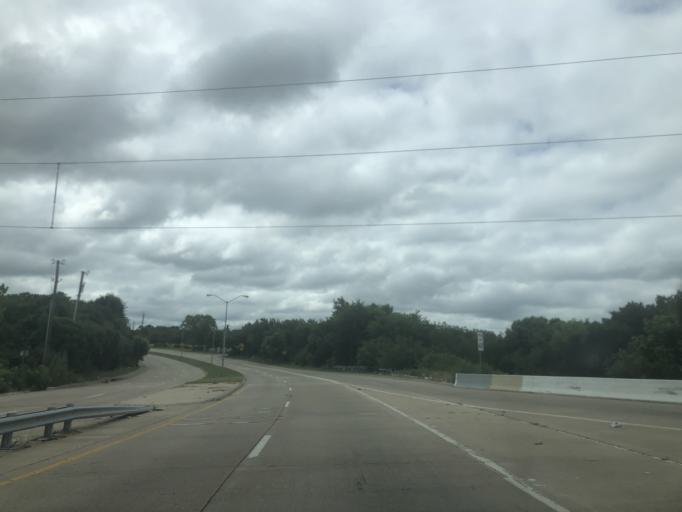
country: US
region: Texas
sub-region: Dallas County
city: Duncanville
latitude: 32.6691
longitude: -96.9472
